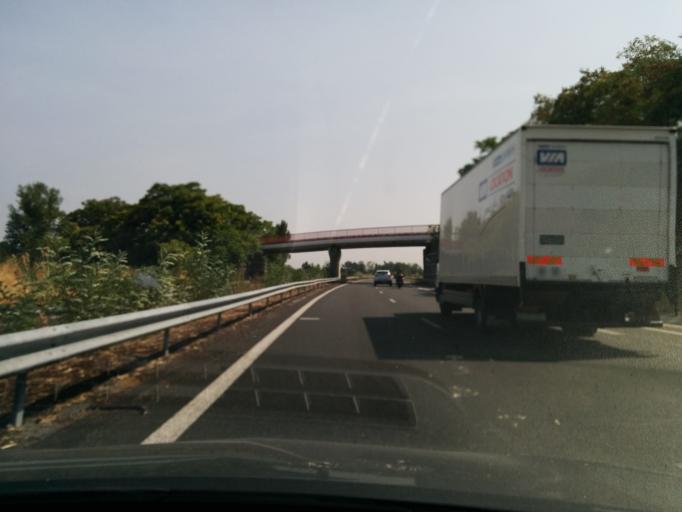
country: FR
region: Midi-Pyrenees
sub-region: Departement du Tarn
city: Brens
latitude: 43.8798
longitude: 1.9103
